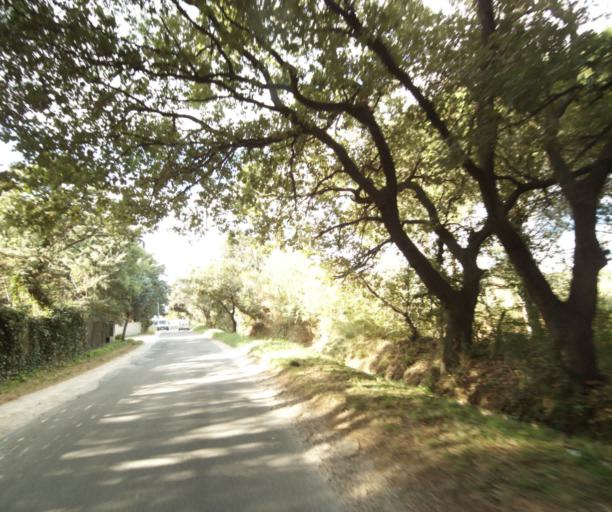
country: FR
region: Languedoc-Roussillon
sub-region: Departement des Pyrenees-Orientales
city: Argelers
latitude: 42.5422
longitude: 3.0409
